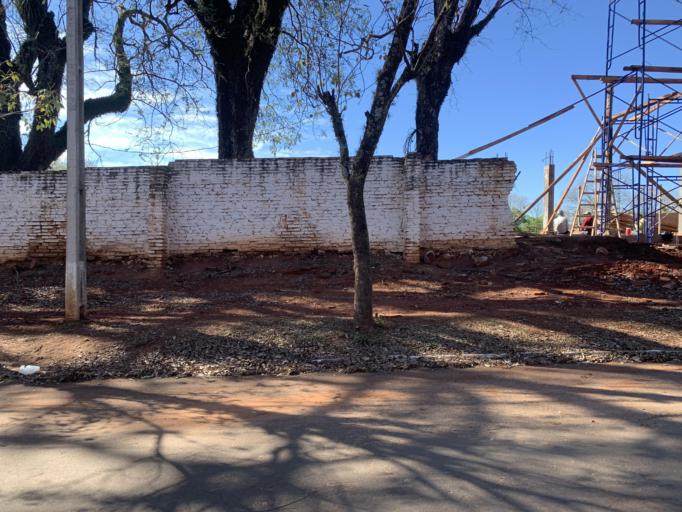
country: PY
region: Misiones
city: San Juan Bautista
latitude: -26.6670
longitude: -57.1408
